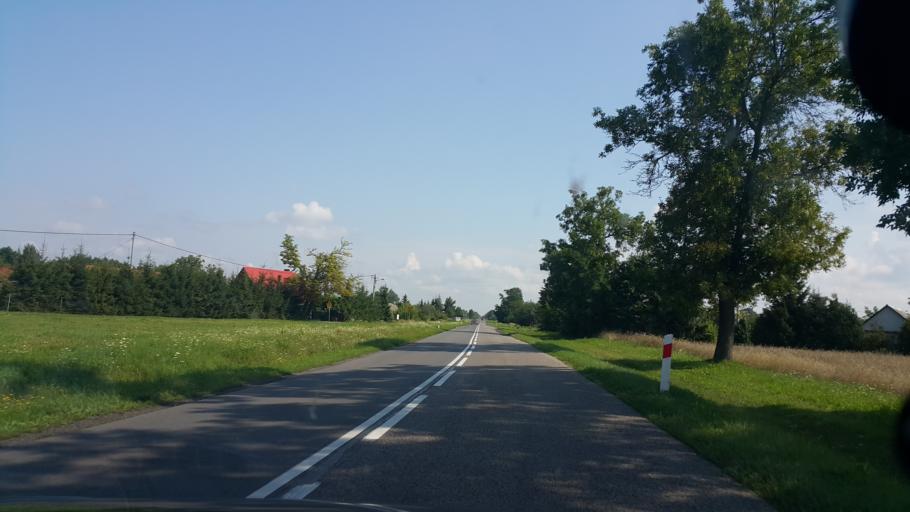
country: PL
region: Lublin Voivodeship
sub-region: Powiat wlodawski
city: Urszulin
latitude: 51.3731
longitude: 23.1827
